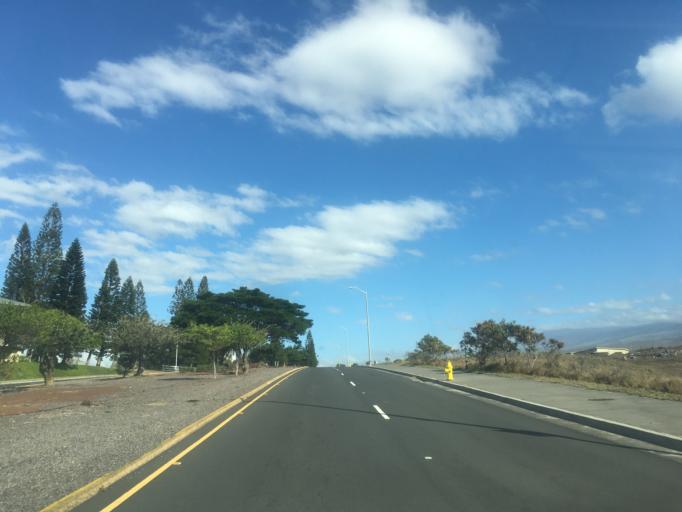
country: US
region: Hawaii
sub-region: Hawaii County
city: Waikoloa
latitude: 19.9255
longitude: -155.7937
